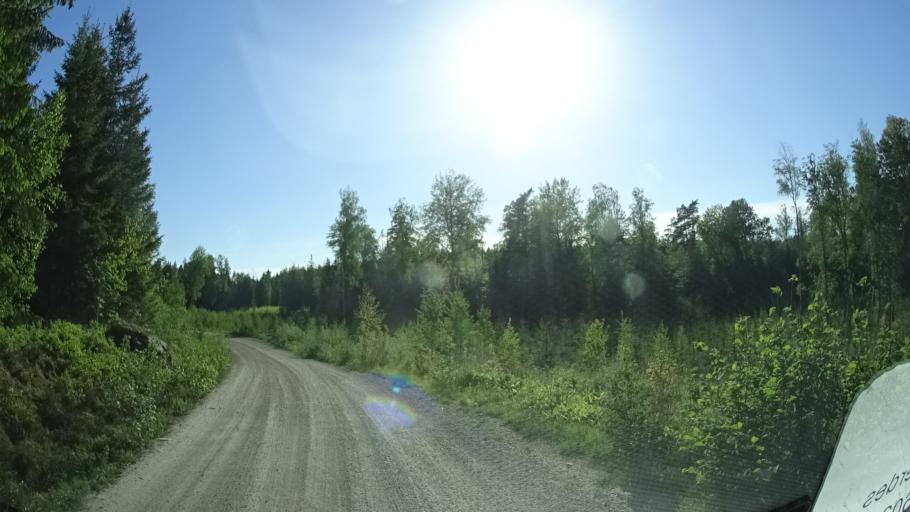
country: SE
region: OEstergoetland
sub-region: Finspangs Kommun
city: Finspang
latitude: 58.6151
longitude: 15.6930
